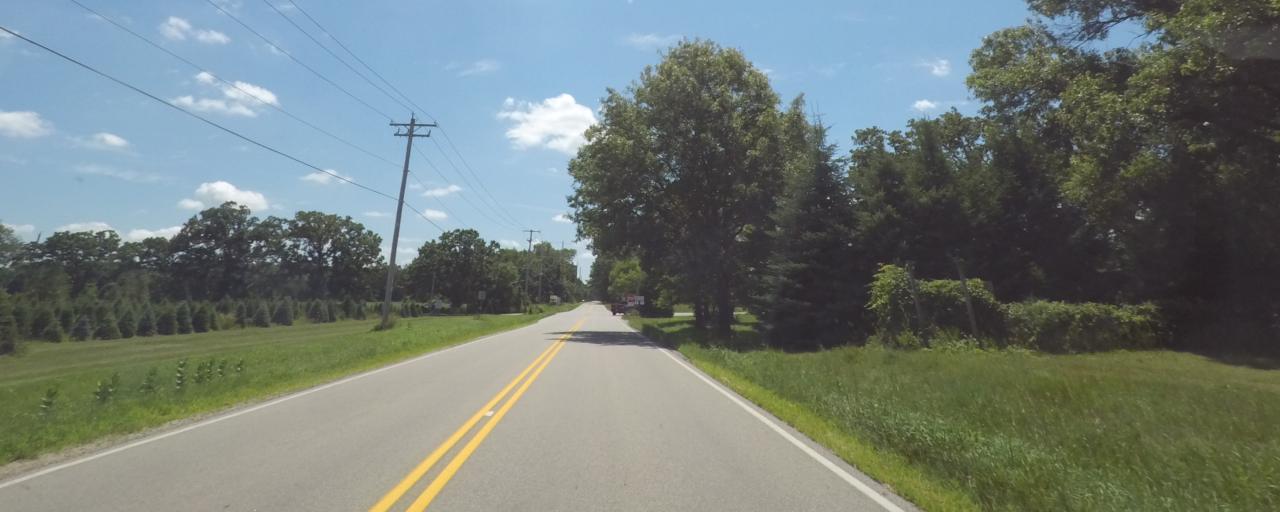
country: US
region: Wisconsin
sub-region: Waukesha County
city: Eagle
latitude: 42.9389
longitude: -88.4983
